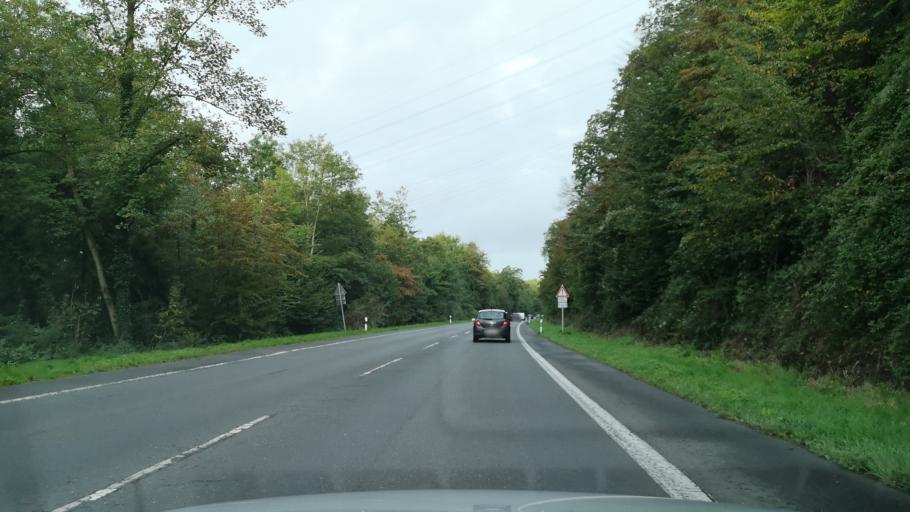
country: DE
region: North Rhine-Westphalia
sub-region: Regierungsbezirk Arnsberg
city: Hagen
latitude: 51.3990
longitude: 7.5035
